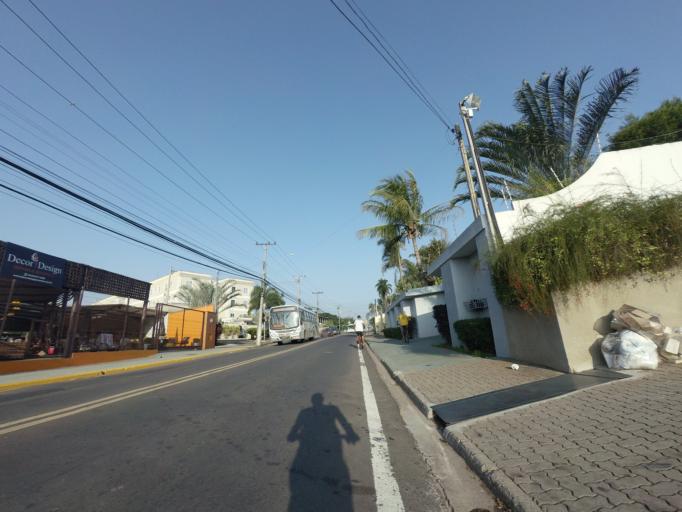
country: BR
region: Sao Paulo
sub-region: Piracicaba
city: Piracicaba
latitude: -22.7413
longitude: -47.6102
